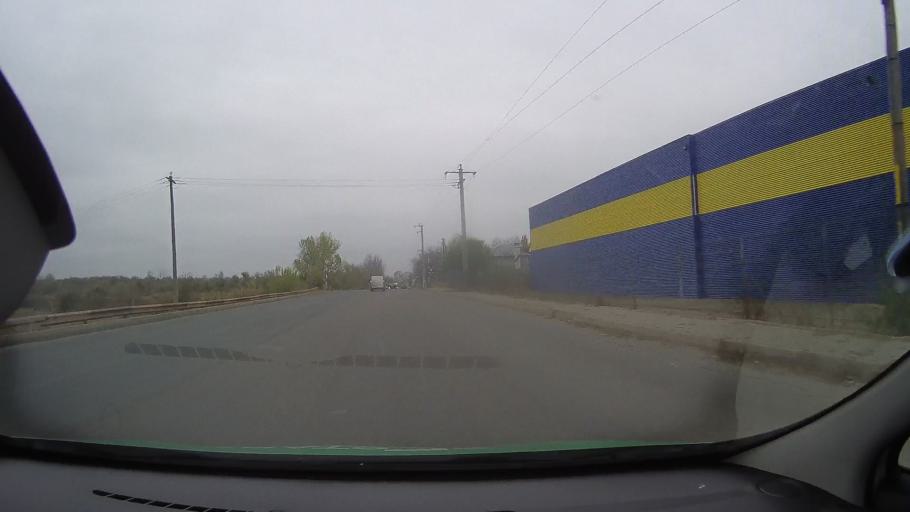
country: RO
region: Ialomita
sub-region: Comuna Slobozia
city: Slobozia
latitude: 44.5772
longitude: 27.3869
